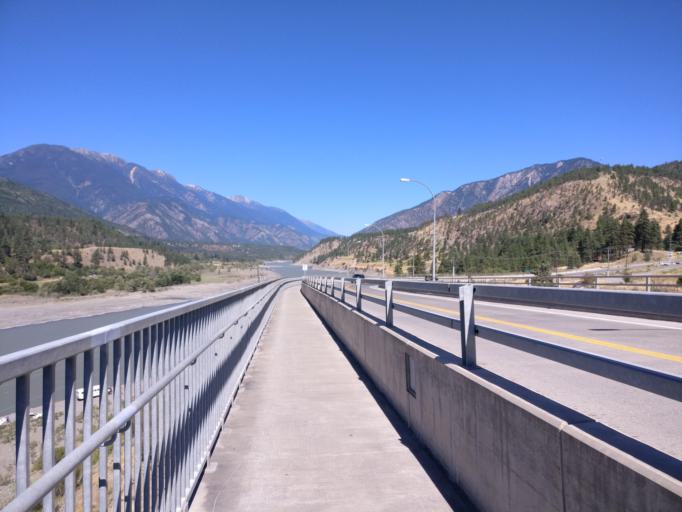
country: CA
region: British Columbia
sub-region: Thompson-Nicola Regional District
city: Ashcroft
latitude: 50.2362
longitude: -121.5812
